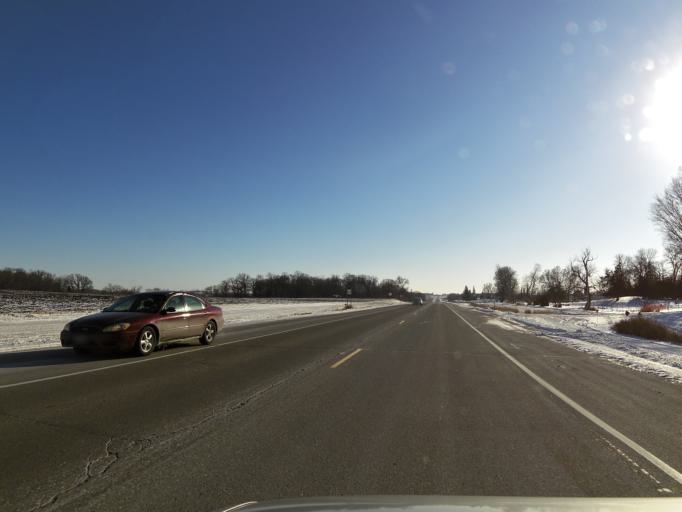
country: US
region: Minnesota
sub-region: Le Sueur County
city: New Prague
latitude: 44.6304
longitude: -93.5017
